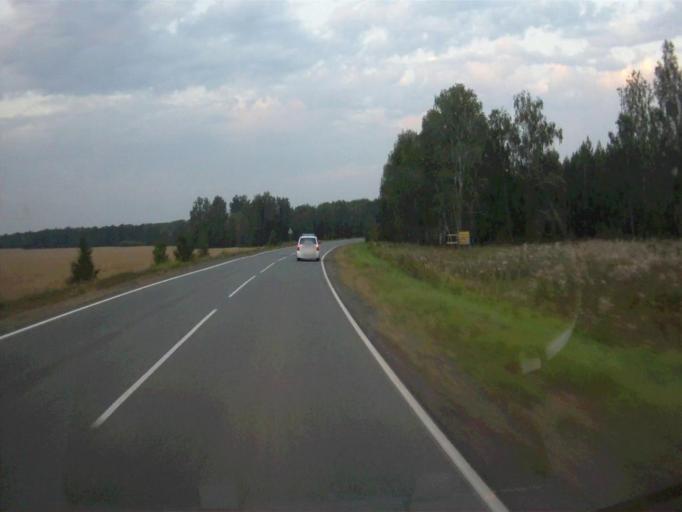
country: RU
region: Chelyabinsk
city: Chebarkul'
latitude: 55.1750
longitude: 60.4547
